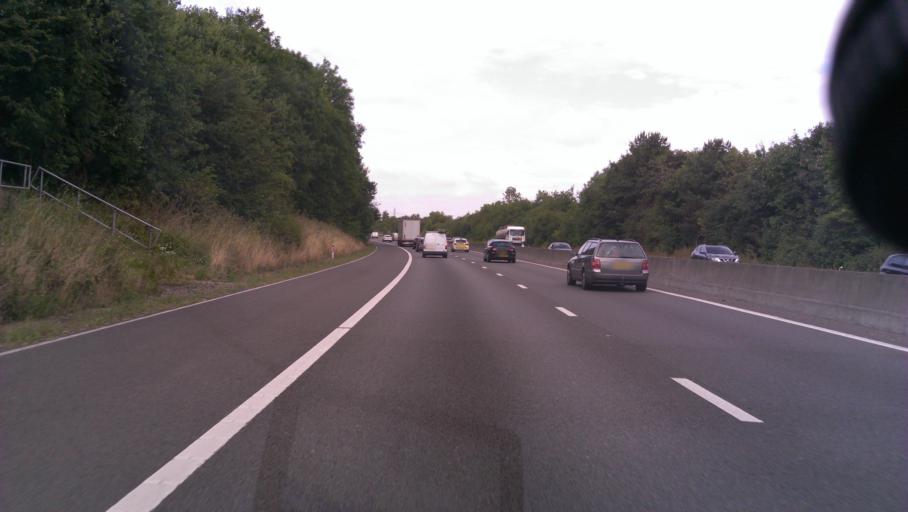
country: GB
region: England
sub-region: Essex
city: Elsenham
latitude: 51.9313
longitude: 0.2246
